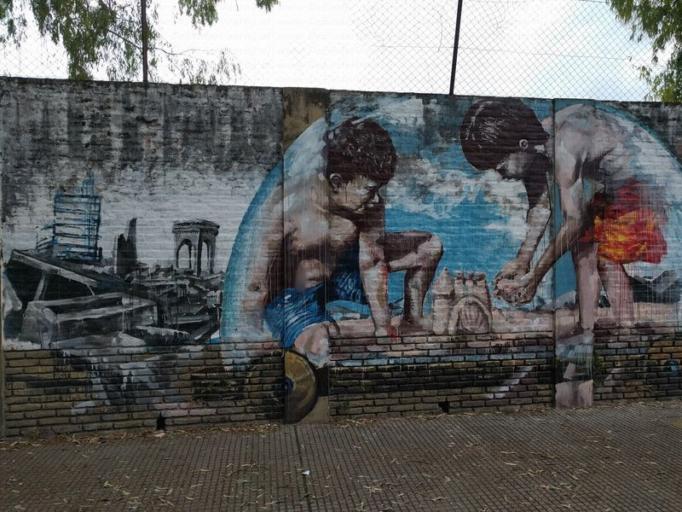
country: AR
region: Buenos Aires F.D.
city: Colegiales
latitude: -34.5591
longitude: -58.4794
